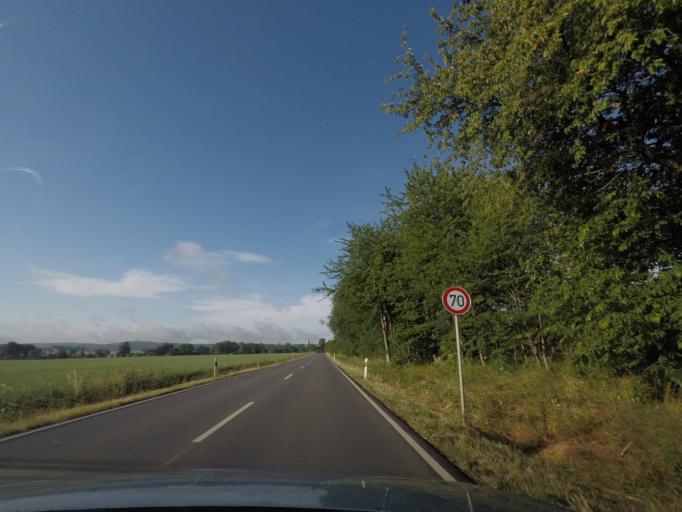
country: DE
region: Saxony-Anhalt
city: Huy-Neinstedt
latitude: 51.9942
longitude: 10.8937
